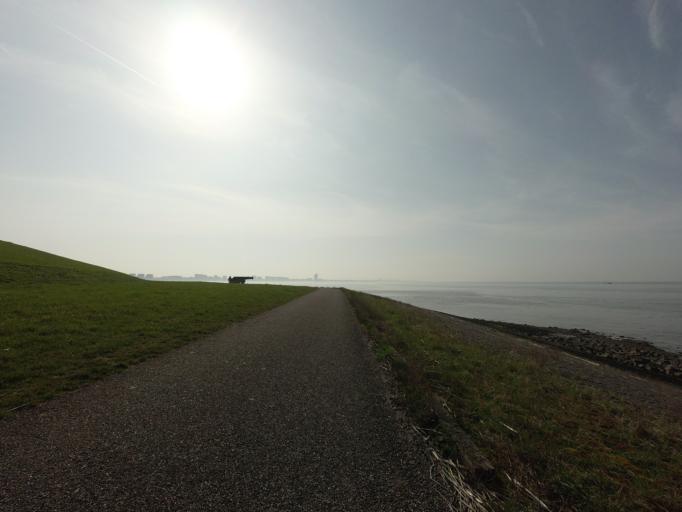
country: NL
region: Zeeland
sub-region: Gemeente Terneuzen
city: Terneuzen
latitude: 51.3461
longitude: 3.8762
